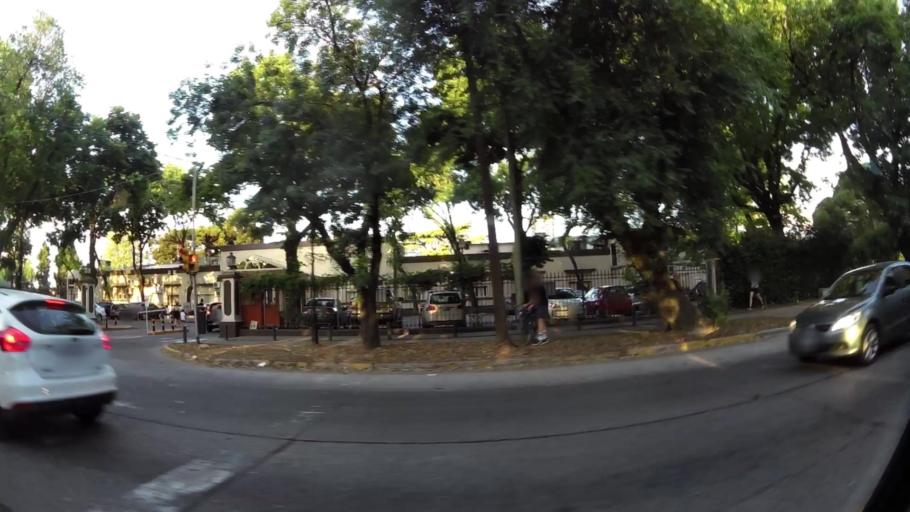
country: AR
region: Buenos Aires
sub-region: Partido de San Isidro
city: San Isidro
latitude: -34.4880
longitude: -58.5254
